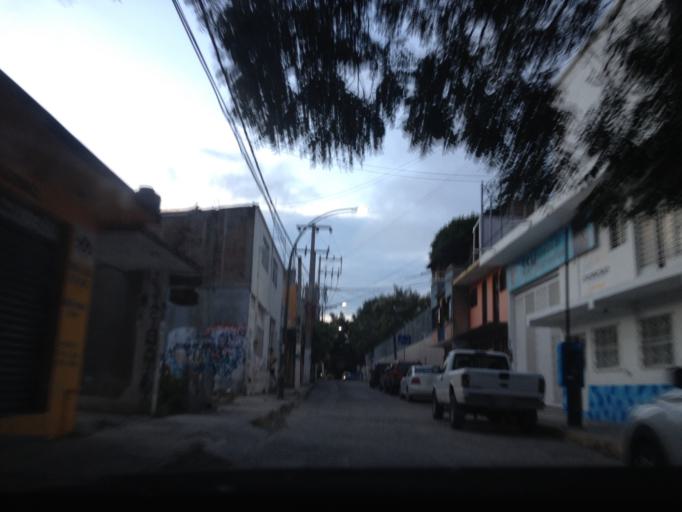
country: MX
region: Guerrero
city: Chilpancingo de los Bravos
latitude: 17.5584
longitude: -99.5045
